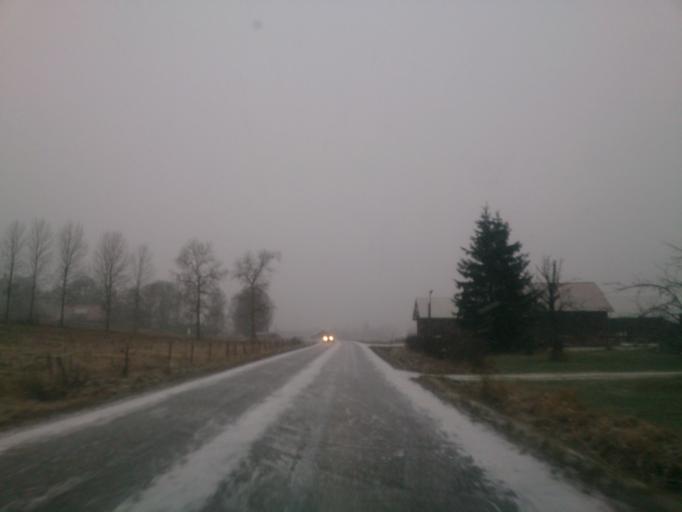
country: SE
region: OEstergoetland
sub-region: Soderkopings Kommun
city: Soederkoeping
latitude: 58.4854
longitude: 16.3032
